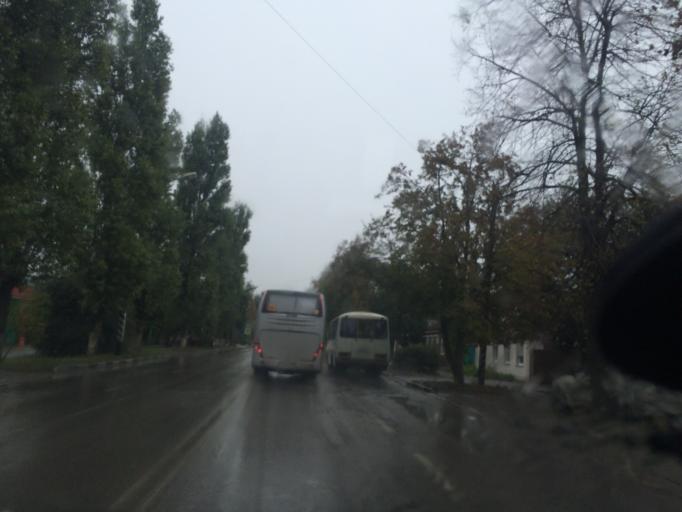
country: RU
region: Rostov
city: Azov
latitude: 47.0966
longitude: 39.4452
